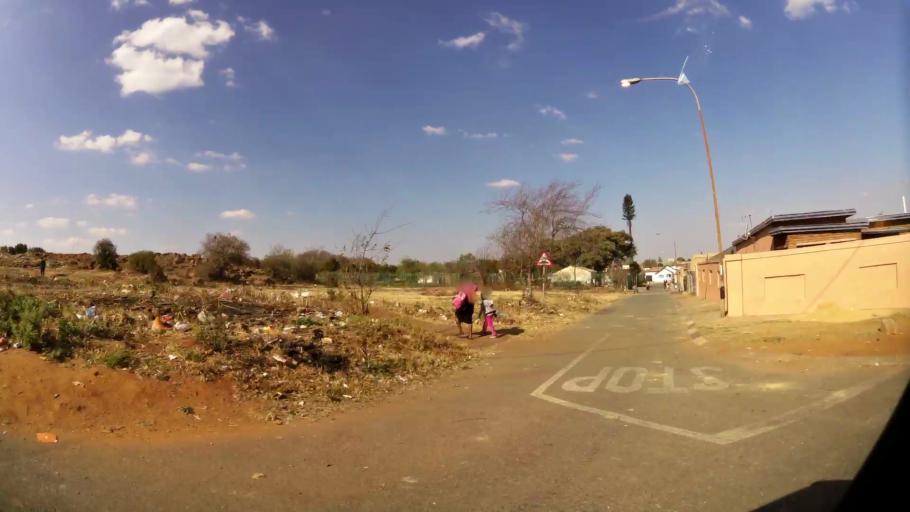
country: ZA
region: Gauteng
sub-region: City of Johannesburg Metropolitan Municipality
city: Soweto
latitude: -26.2207
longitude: 27.8892
